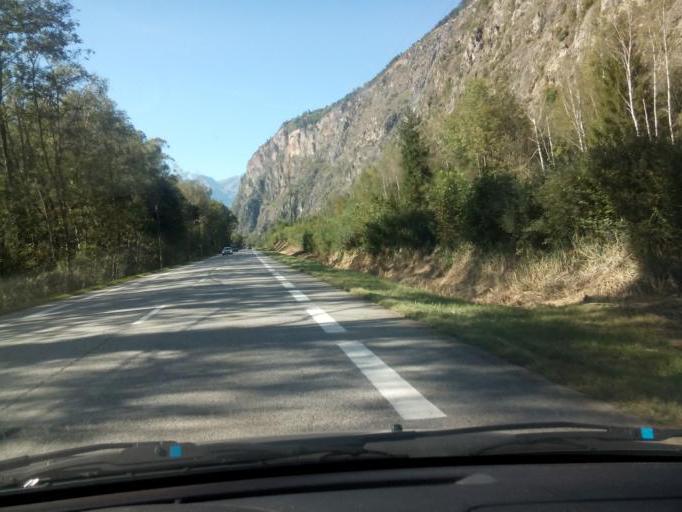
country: FR
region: Rhone-Alpes
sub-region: Departement de l'Isere
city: Huez
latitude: 45.0398
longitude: 6.0615
